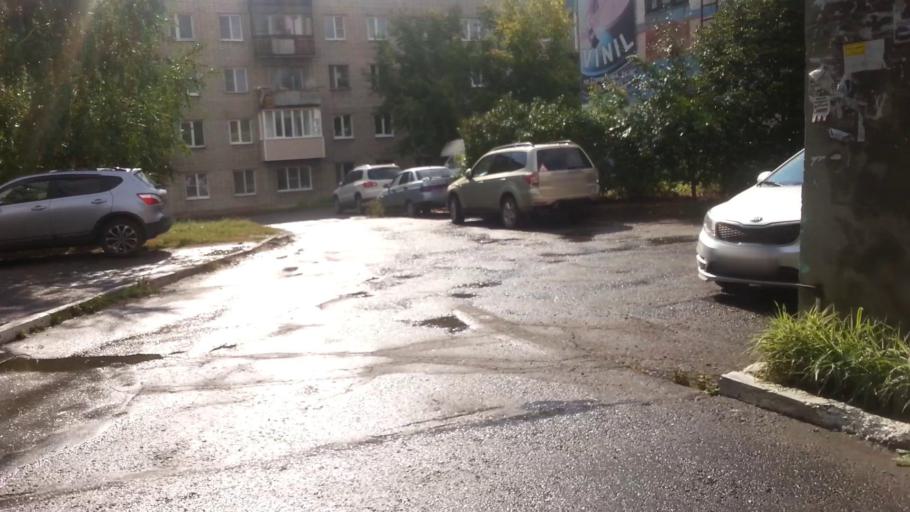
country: RU
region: Altai Krai
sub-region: Gorod Barnaulskiy
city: Barnaul
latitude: 53.3465
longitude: 83.7573
